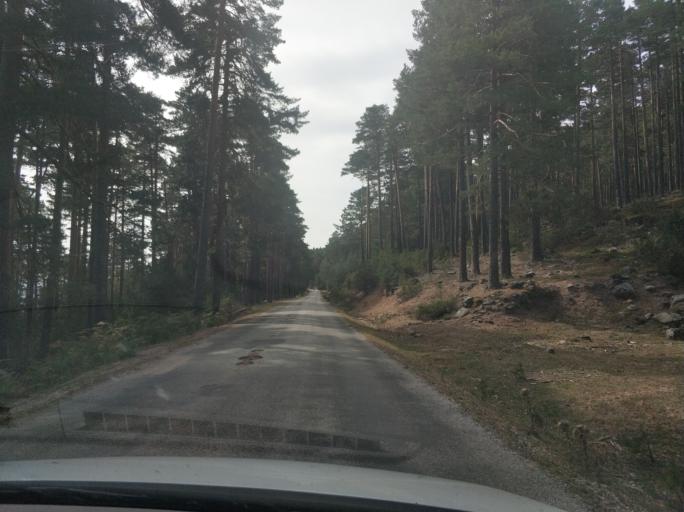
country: ES
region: Castille and Leon
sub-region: Provincia de Soria
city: Duruelo de la Sierra
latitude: 41.9958
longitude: -2.9232
